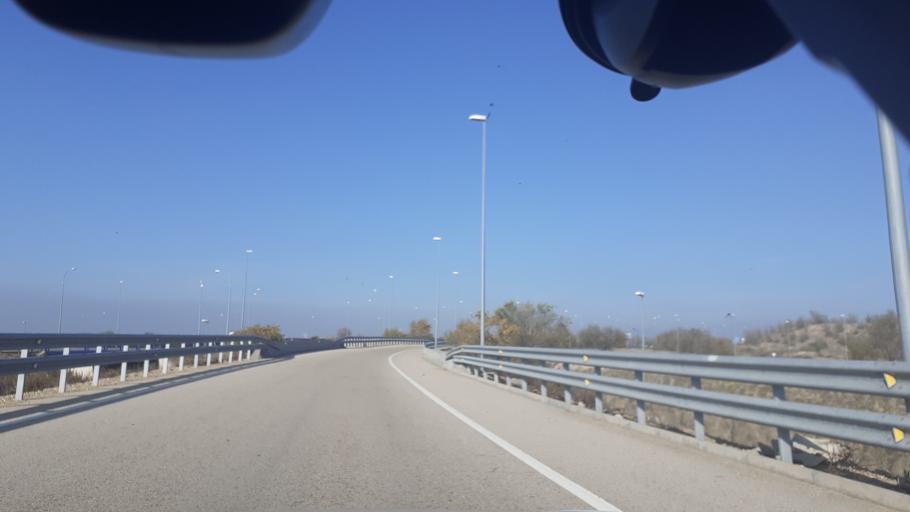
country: ES
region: Madrid
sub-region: Provincia de Madrid
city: Coslada
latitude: 40.4018
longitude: -3.5718
